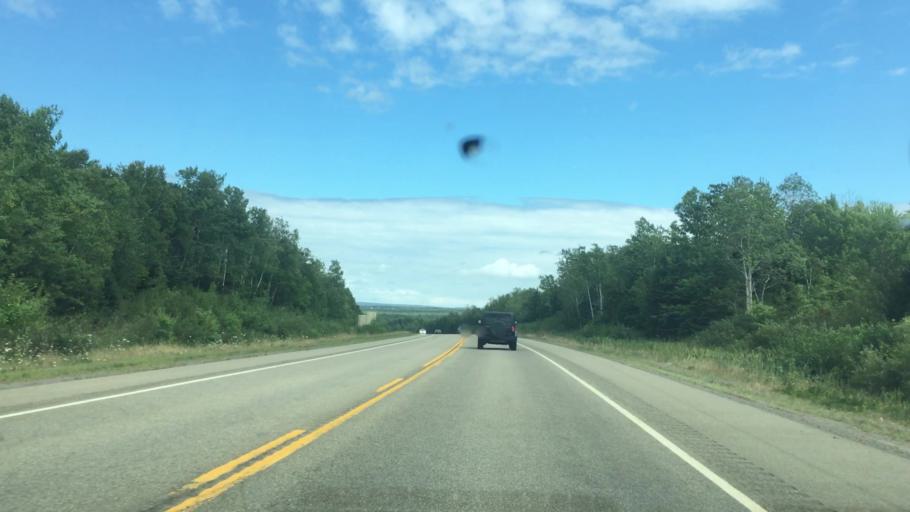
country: CA
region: Nova Scotia
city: Port Hawkesbury
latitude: 45.6309
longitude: -61.5896
